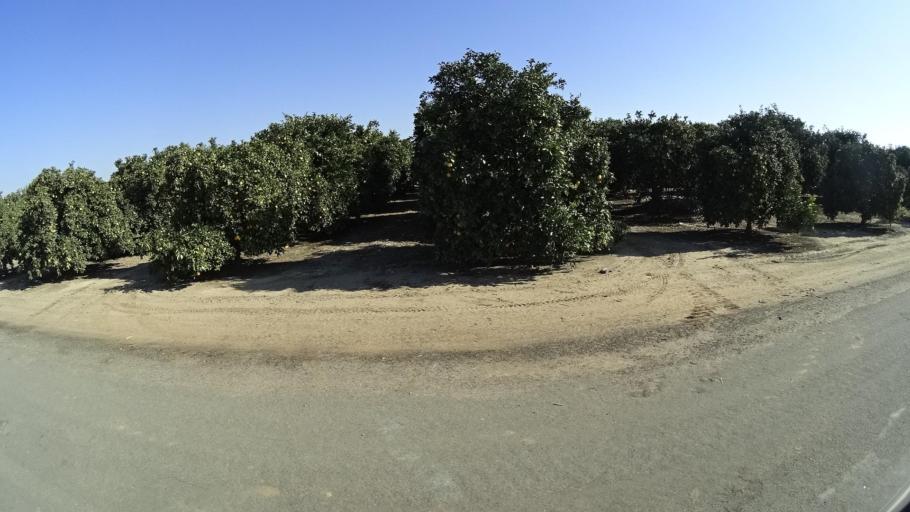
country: US
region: California
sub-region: Tulare County
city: Richgrove
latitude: 35.7341
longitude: -119.1430
